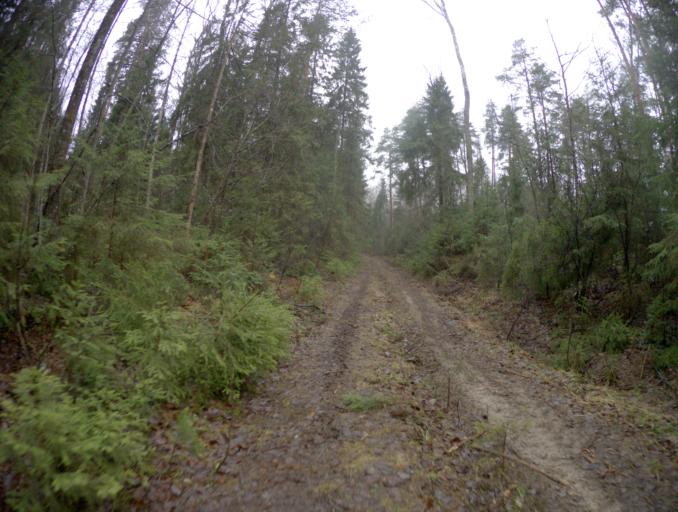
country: RU
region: Vladimir
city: Golovino
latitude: 56.0063
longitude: 40.4796
